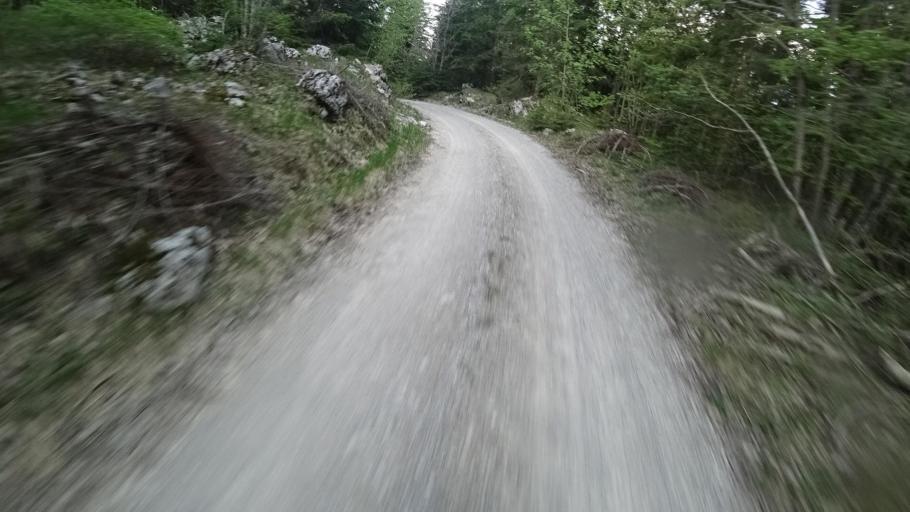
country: BA
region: Federation of Bosnia and Herzegovina
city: Glamoc
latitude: 44.1337
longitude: 16.7052
